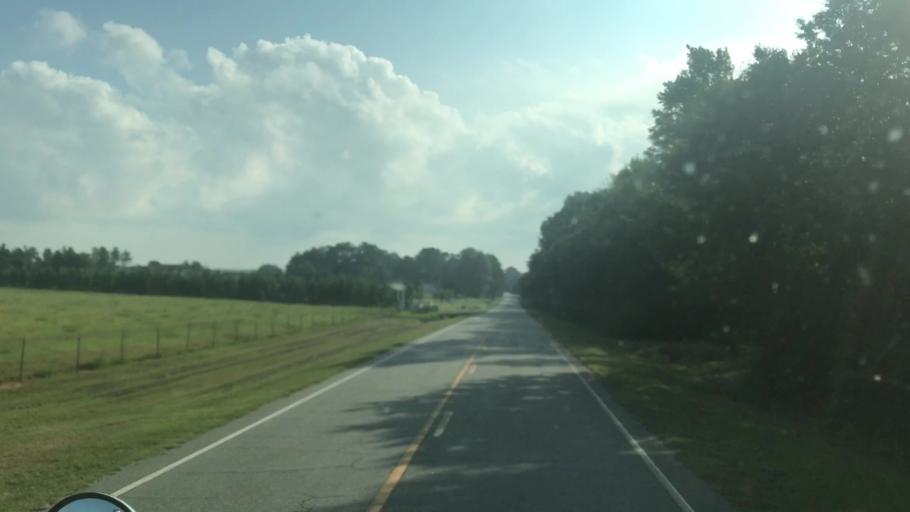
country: US
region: Florida
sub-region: Gadsden County
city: Havana
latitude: 30.7104
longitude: -84.5041
